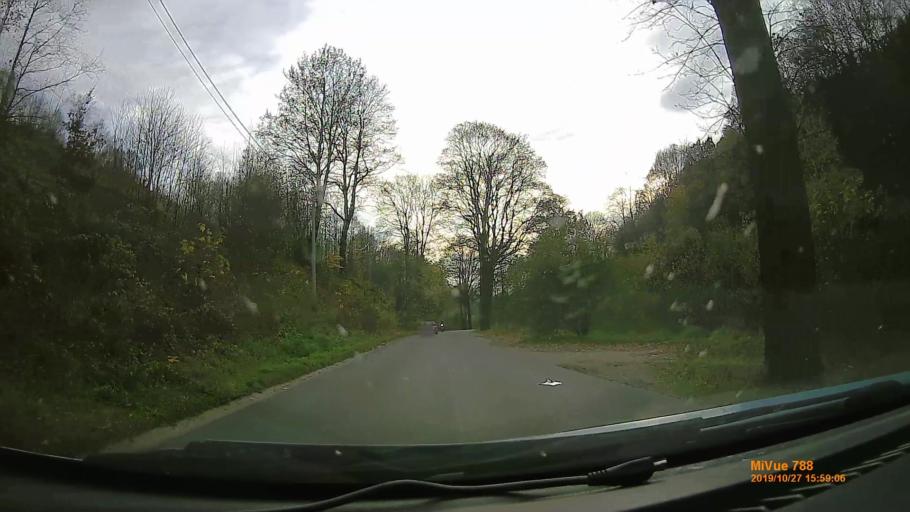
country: PL
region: Lower Silesian Voivodeship
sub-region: Powiat klodzki
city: Nowa Ruda
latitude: 50.5381
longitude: 16.5254
